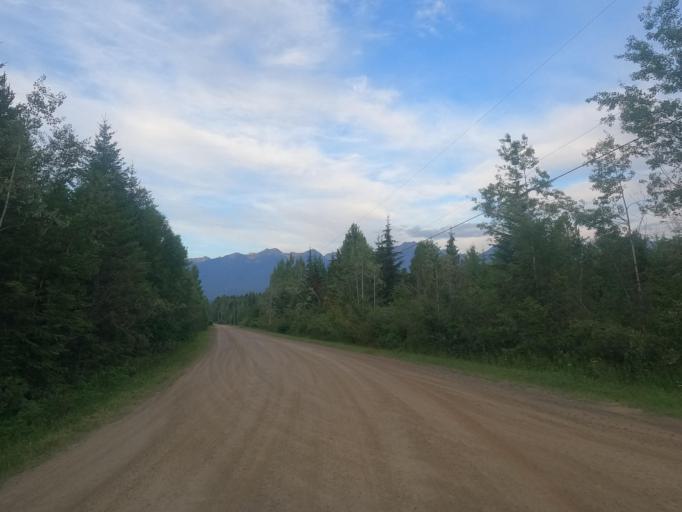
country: CA
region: British Columbia
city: Golden
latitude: 51.4456
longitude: -117.0362
